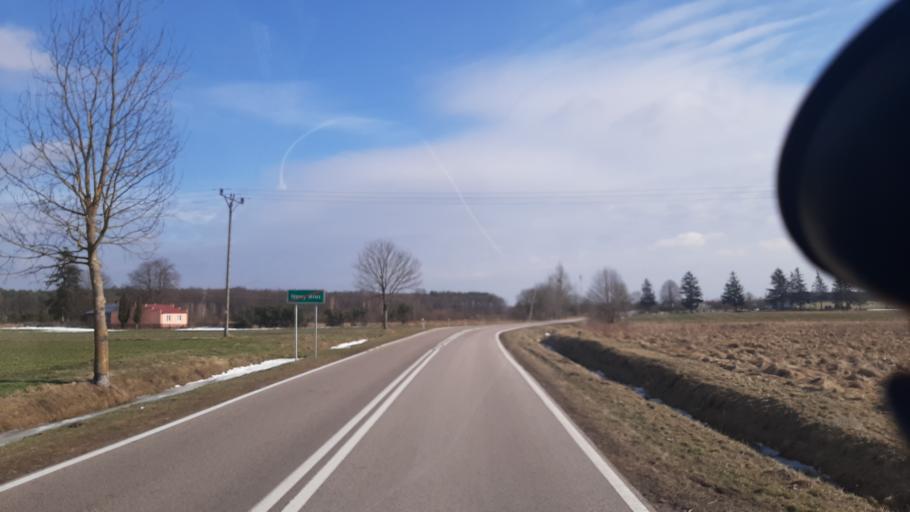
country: PL
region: Lublin Voivodeship
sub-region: Powiat wlodawski
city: Hansk
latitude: 51.4757
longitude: 23.3085
